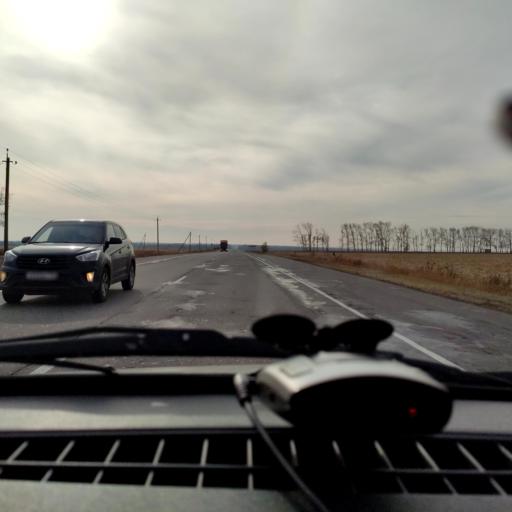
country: RU
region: Voronezj
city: Strelitsa
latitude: 51.5348
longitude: 38.9698
